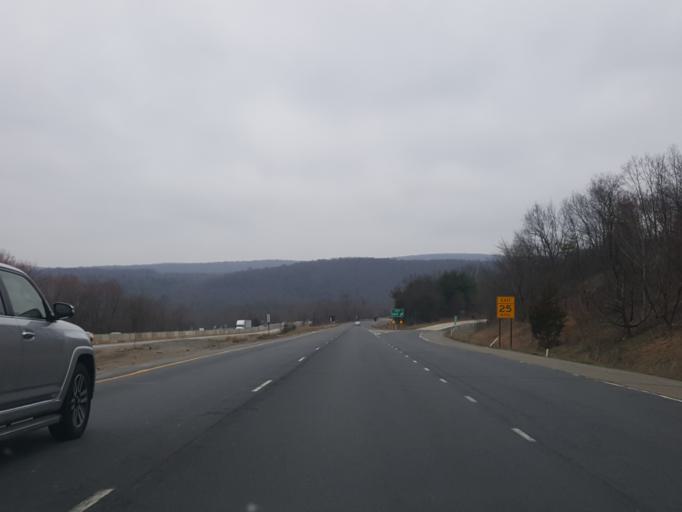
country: US
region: Pennsylvania
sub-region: Schuylkill County
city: Pine Grove
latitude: 40.5393
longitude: -76.4296
